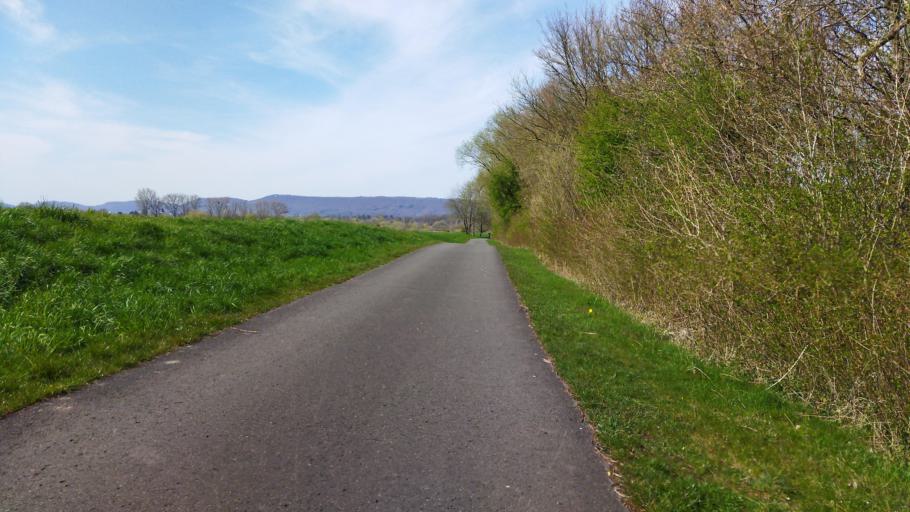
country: DE
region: Lower Saxony
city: Hessisch Oldendorf
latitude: 52.1559
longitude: 9.2710
